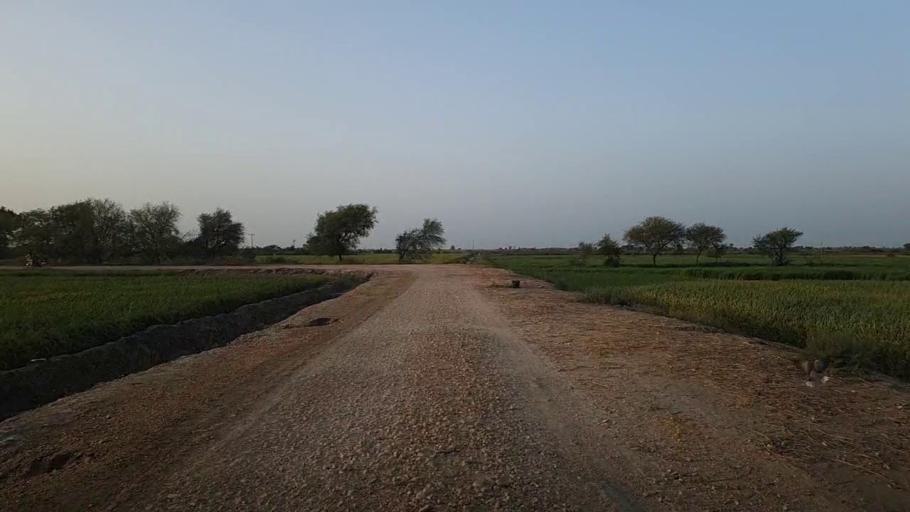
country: PK
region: Sindh
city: Kario
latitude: 24.7237
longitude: 68.4629
